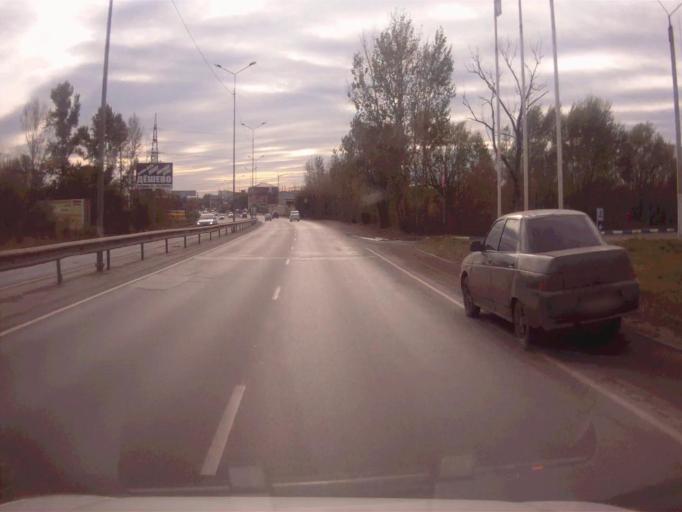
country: RU
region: Chelyabinsk
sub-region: Gorod Chelyabinsk
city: Chelyabinsk
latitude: 55.1133
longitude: 61.4122
